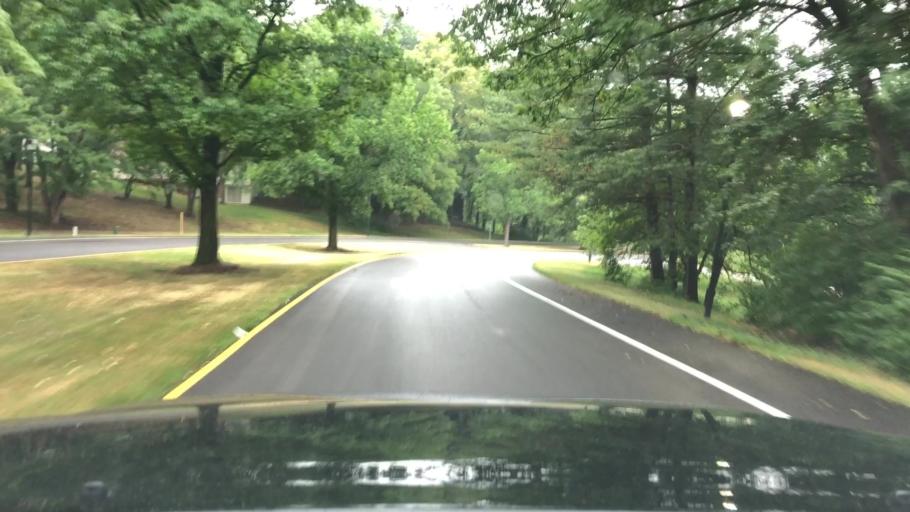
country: US
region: Missouri
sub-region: Saint Charles County
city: Lake Saint Louis
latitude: 38.8026
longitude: -90.7928
